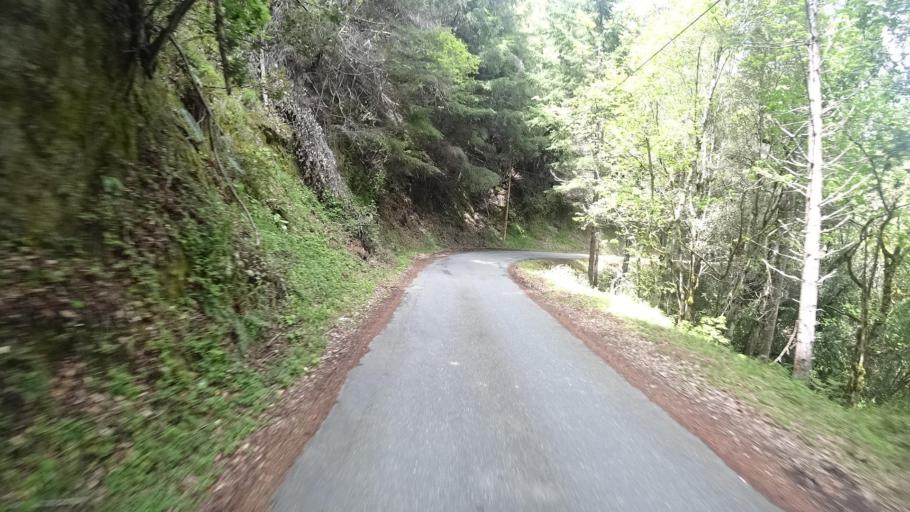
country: US
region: California
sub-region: Humboldt County
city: Blue Lake
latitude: 40.7656
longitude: -123.9345
